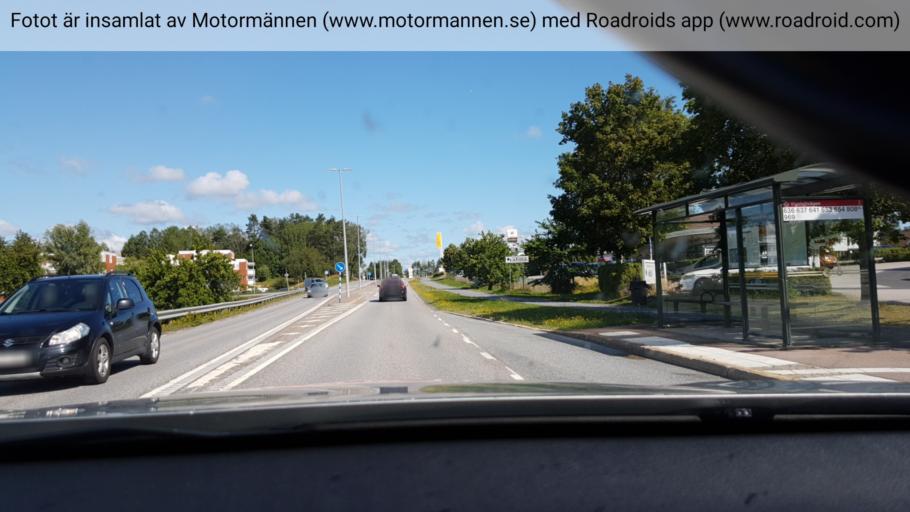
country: SE
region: Stockholm
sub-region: Norrtalje Kommun
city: Norrtalje
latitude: 59.7621
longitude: 18.6902
